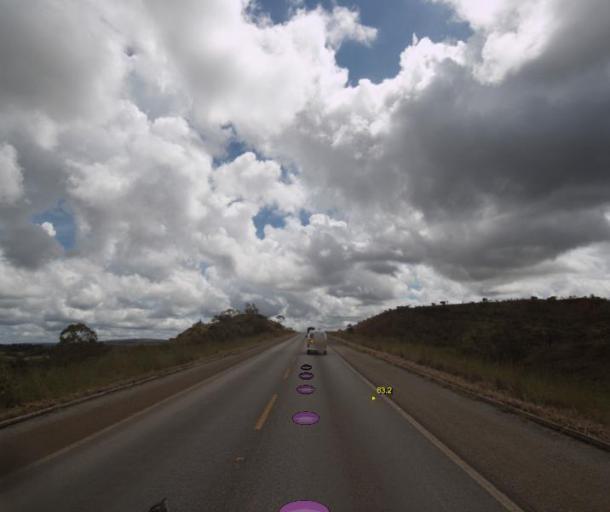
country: BR
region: Goias
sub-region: Pirenopolis
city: Pirenopolis
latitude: -15.7610
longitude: -48.7338
